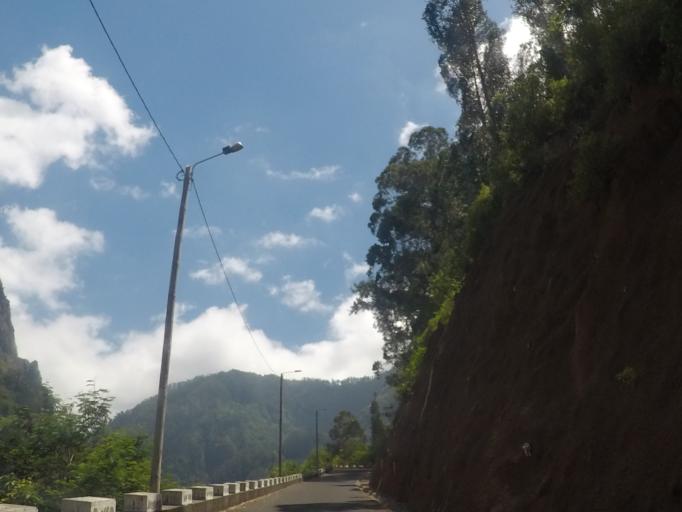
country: PT
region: Madeira
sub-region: Camara de Lobos
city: Curral das Freiras
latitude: 32.7177
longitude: -16.9698
